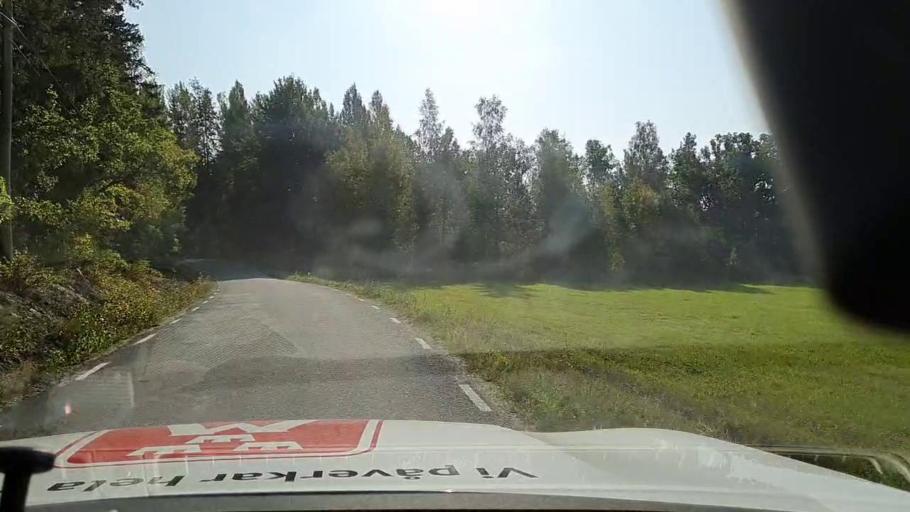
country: SE
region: Soedermanland
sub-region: Eskilstuna Kommun
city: Kvicksund
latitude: 59.3211
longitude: 16.2443
